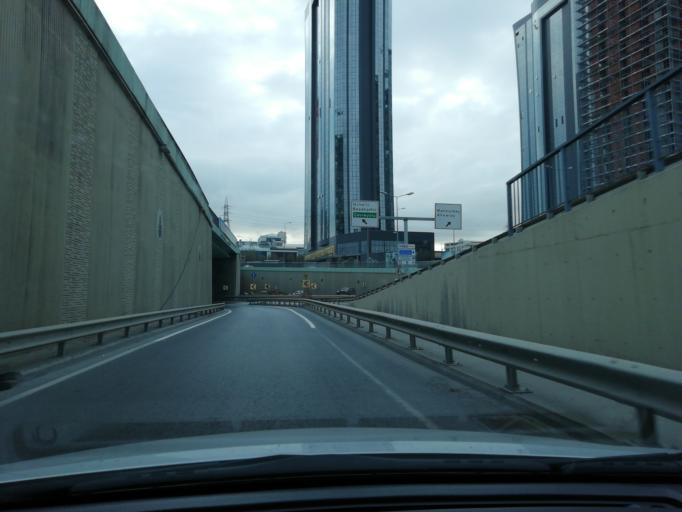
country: TR
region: Istanbul
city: Mahmutbey
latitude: 41.0455
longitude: 28.8100
